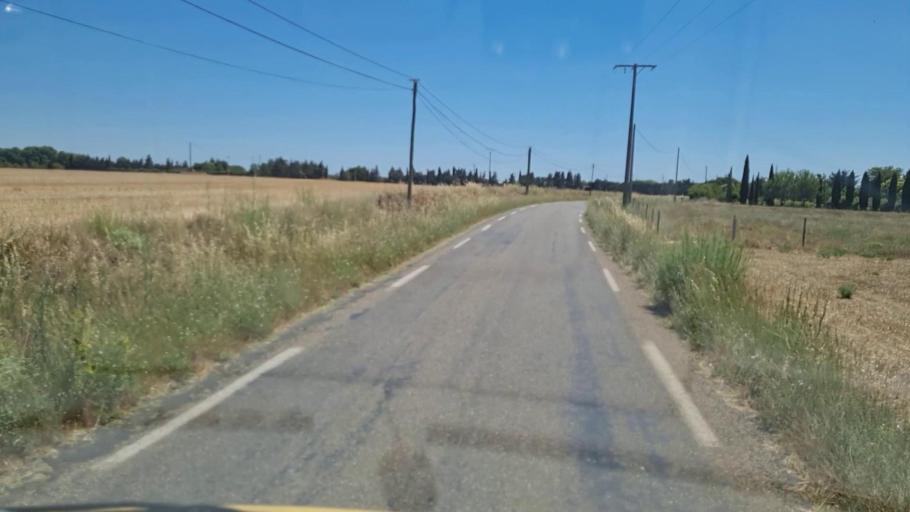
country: FR
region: Languedoc-Roussillon
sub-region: Departement du Gard
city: Le Cailar
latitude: 43.6959
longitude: 4.2327
